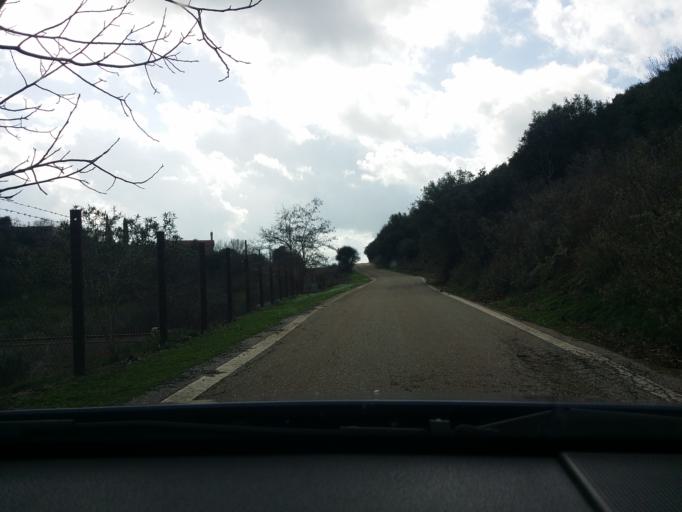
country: GR
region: West Greece
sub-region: Nomos Aitolias kai Akarnanias
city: Fitiai
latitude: 38.6502
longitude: 21.1992
